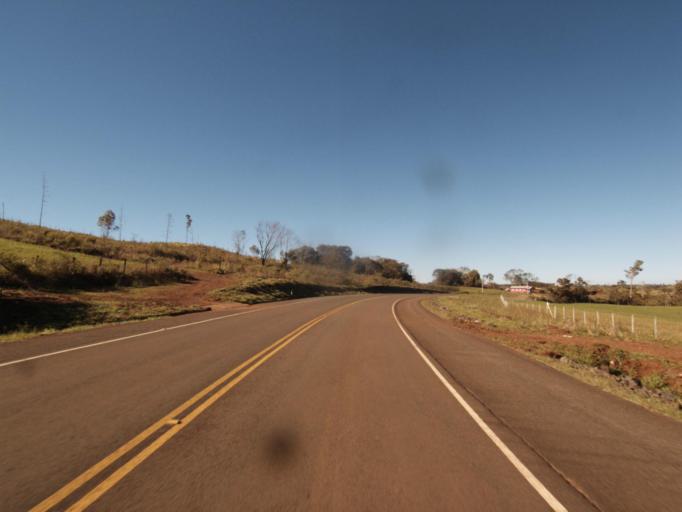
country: AR
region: Misiones
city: Bernardo de Irigoyen
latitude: -26.6100
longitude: -53.6927
